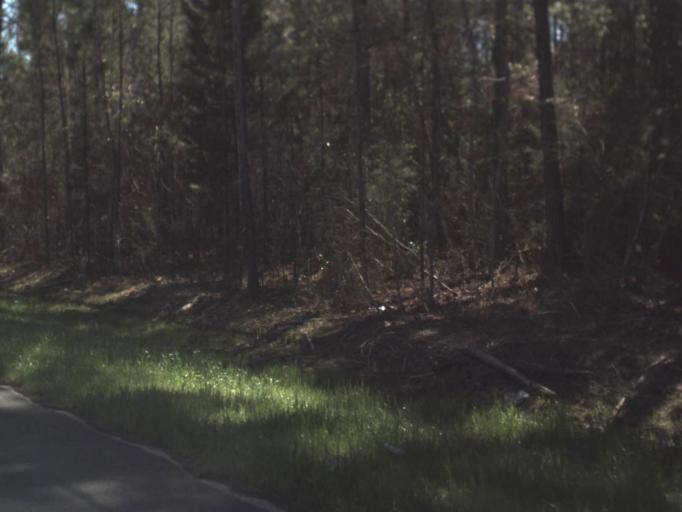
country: US
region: Florida
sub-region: Jackson County
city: Marianna
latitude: 30.7935
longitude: -85.2669
